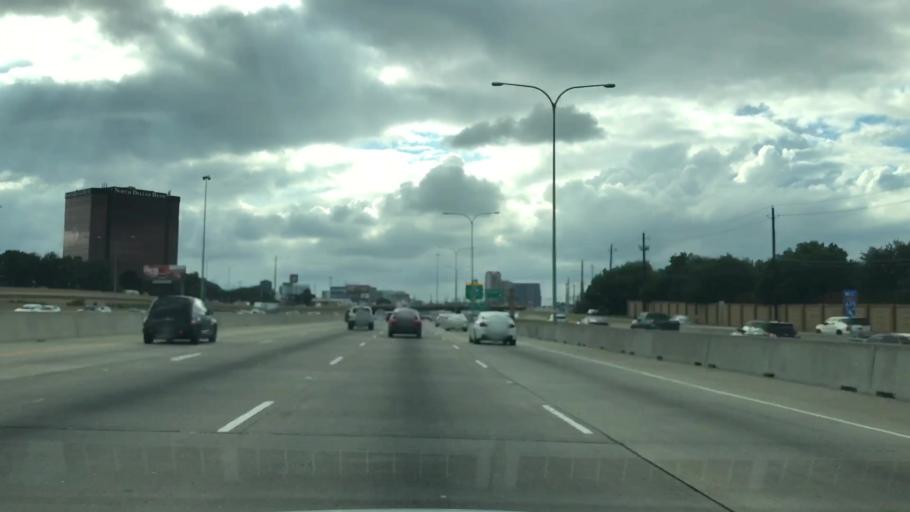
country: US
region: Texas
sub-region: Dallas County
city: Addison
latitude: 32.9256
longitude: -96.7985
